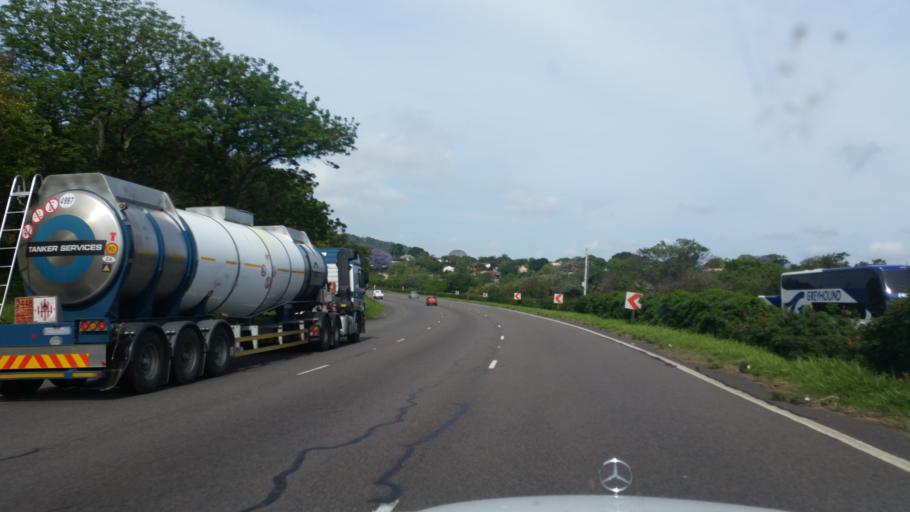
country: ZA
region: KwaZulu-Natal
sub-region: eThekwini Metropolitan Municipality
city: Berea
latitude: -29.8384
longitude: 30.8689
